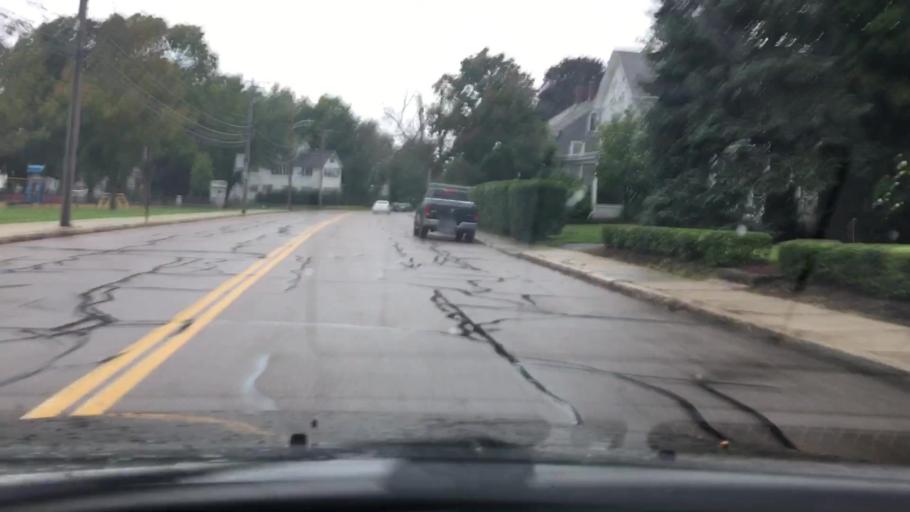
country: US
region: Massachusetts
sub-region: Worcester County
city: Milford
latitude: 42.1445
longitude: -71.5234
